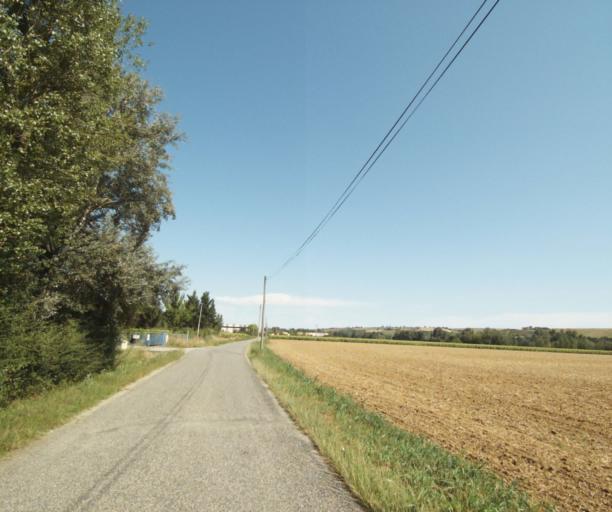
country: FR
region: Midi-Pyrenees
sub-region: Departement de l'Ariege
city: Lezat-sur-Leze
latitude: 43.2867
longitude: 1.3487
